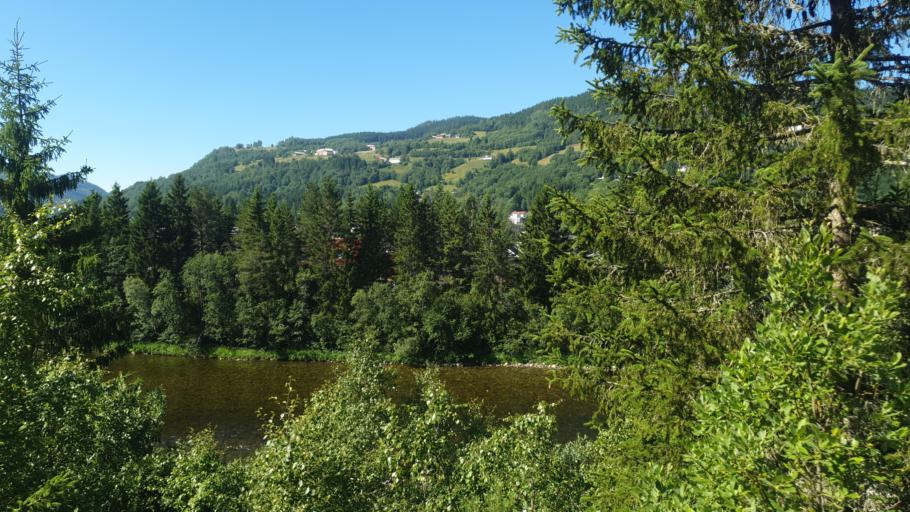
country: NO
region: Sor-Trondelag
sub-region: Meldal
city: Meldal
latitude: 63.1706
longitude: 9.7489
